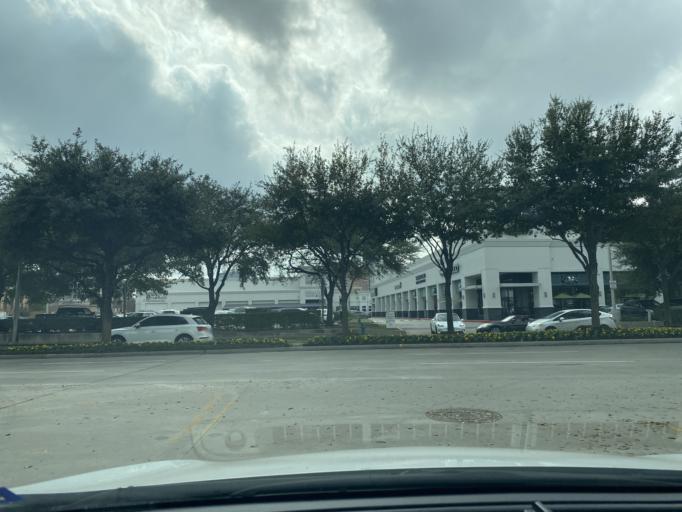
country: US
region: Texas
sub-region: Harris County
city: Hunters Creek Village
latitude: 29.7505
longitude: -95.4599
